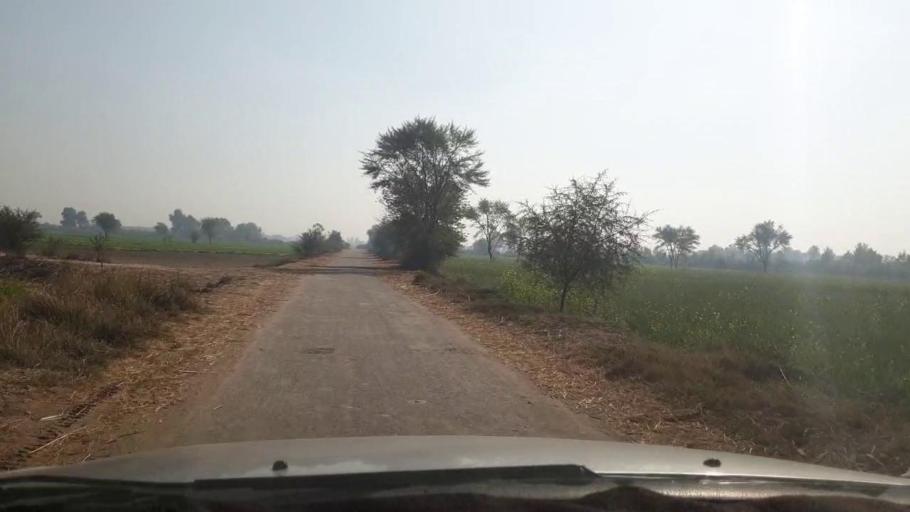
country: PK
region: Sindh
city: Khanpur
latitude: 27.7393
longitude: 69.5064
